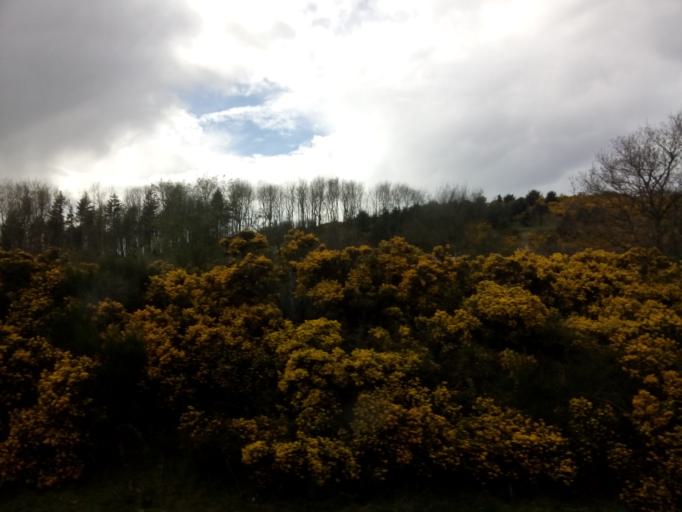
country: GB
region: Scotland
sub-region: The Scottish Borders
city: Duns
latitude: 55.8962
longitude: -2.3287
